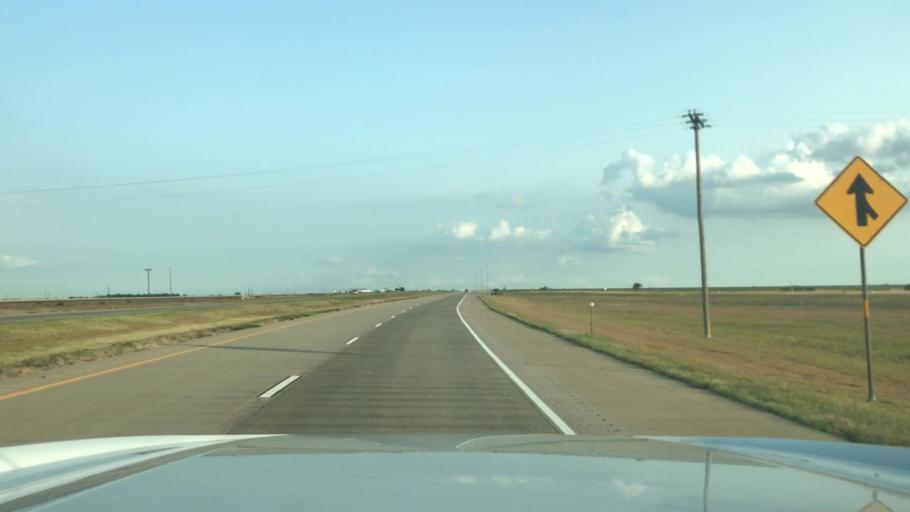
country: US
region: Texas
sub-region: Hale County
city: Seth Ward
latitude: 34.3405
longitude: -101.7441
